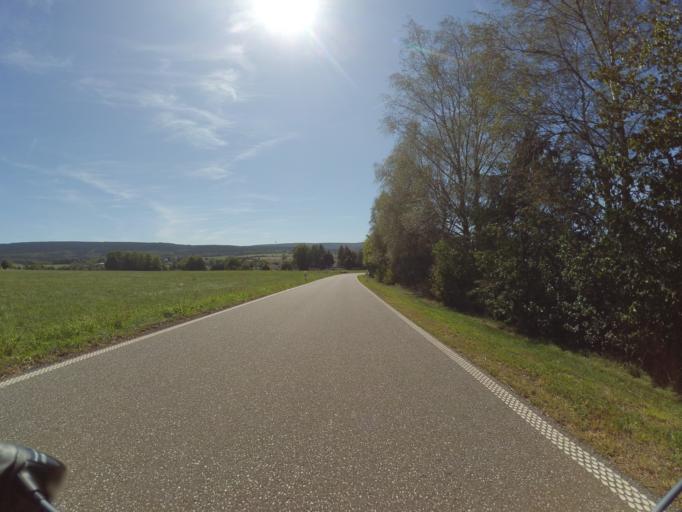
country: DE
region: Rheinland-Pfalz
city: Morbach
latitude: 49.7952
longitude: 7.0931
